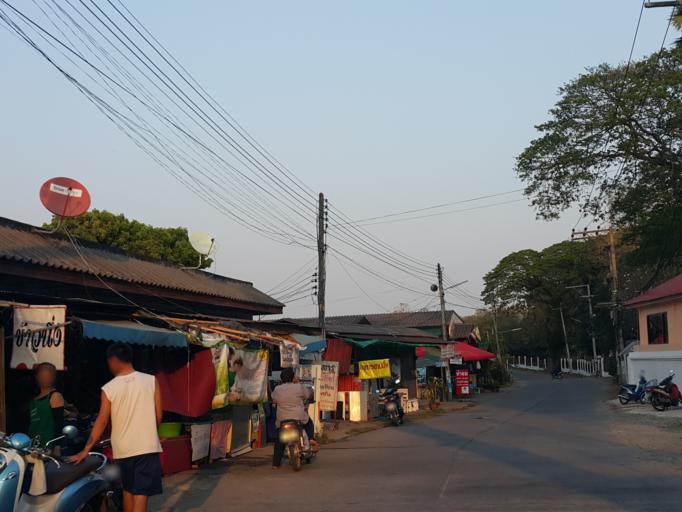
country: TH
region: Chiang Mai
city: San Sai
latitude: 18.8920
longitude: 98.9624
